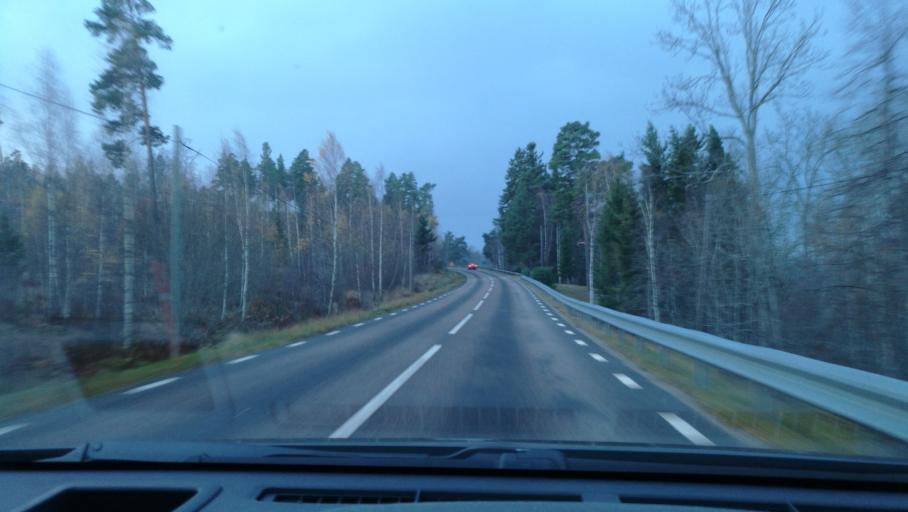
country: SE
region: Soedermanland
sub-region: Vingakers Kommun
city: Vingaker
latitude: 59.1340
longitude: 15.8358
